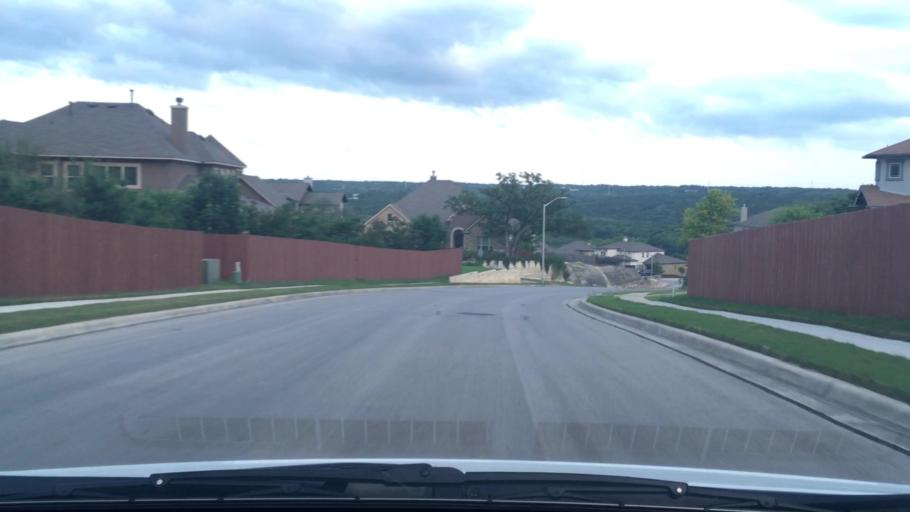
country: US
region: Texas
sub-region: Williamson County
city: Anderson Mill
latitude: 30.4542
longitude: -97.8561
